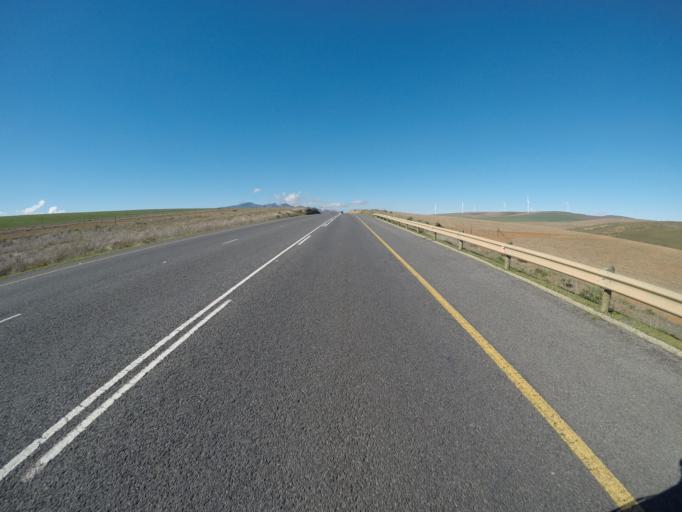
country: ZA
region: Western Cape
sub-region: Overberg District Municipality
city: Caledon
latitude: -34.2118
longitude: 19.3525
